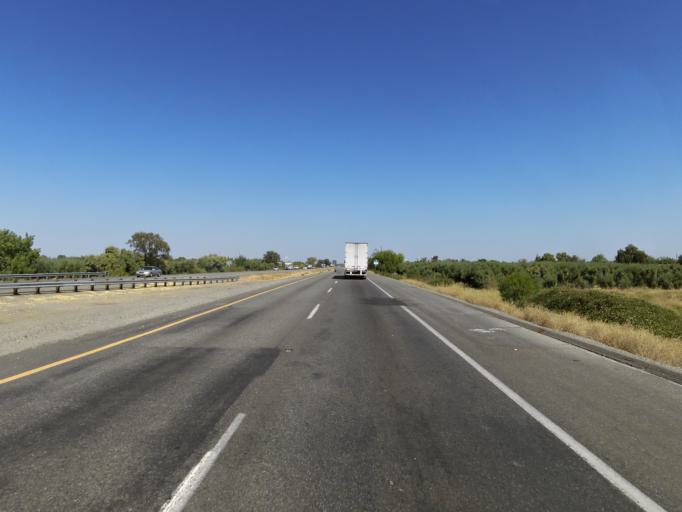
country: US
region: California
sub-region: Tehama County
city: Corning
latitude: 39.9147
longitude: -122.2000
